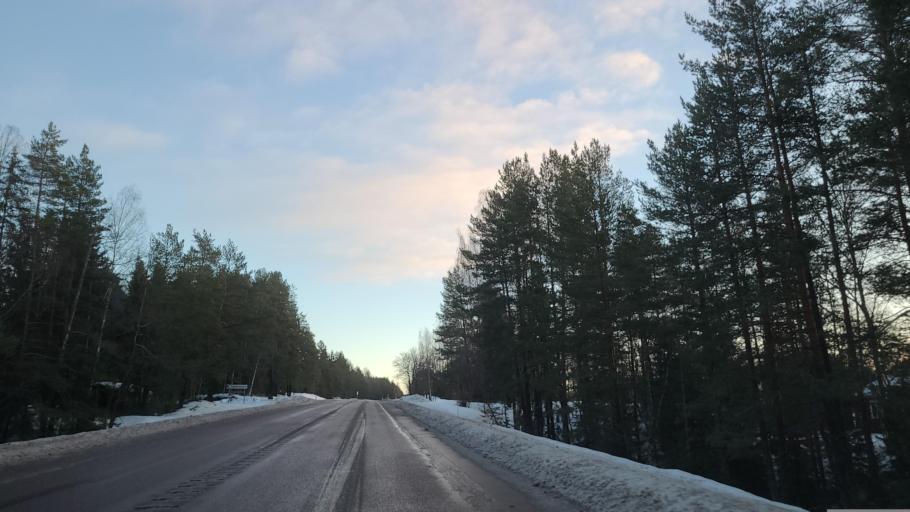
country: SE
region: Gaevleborg
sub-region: Bollnas Kommun
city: Kilafors
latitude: 61.3347
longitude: 16.7453
